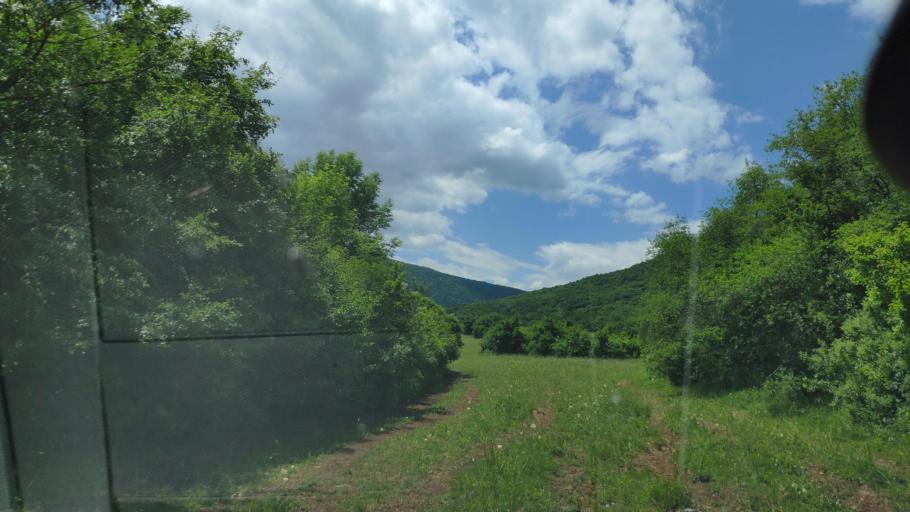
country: SK
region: Kosicky
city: Medzev
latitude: 48.6240
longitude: 20.8825
